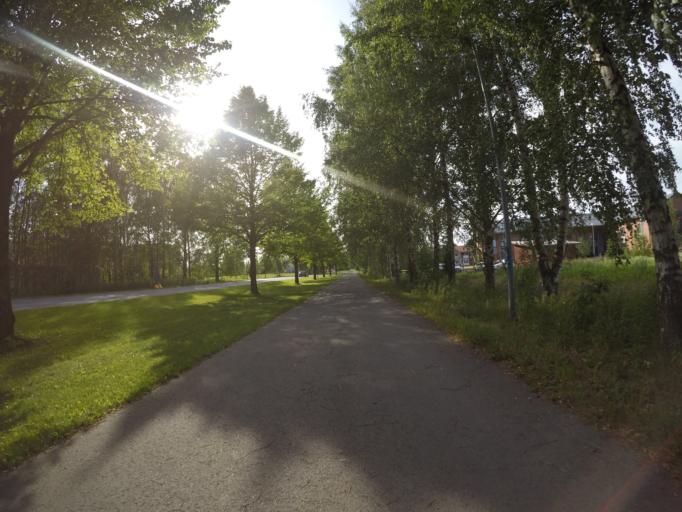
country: FI
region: Haeme
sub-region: Haemeenlinna
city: Haemeenlinna
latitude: 60.9791
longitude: 24.4260
